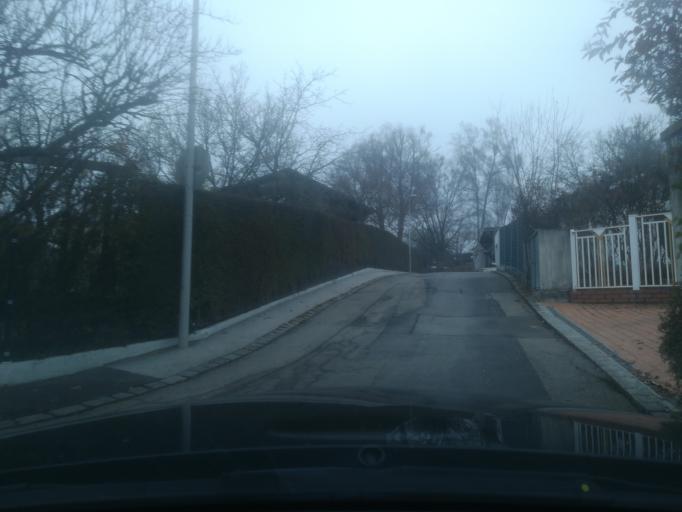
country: AT
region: Upper Austria
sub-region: Linz Stadt
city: Linz
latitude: 48.3269
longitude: 14.2817
